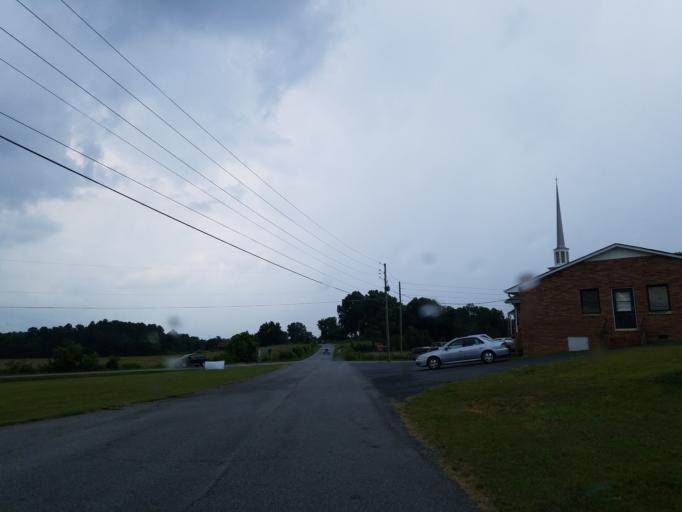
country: US
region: Georgia
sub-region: Bartow County
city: Rydal
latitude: 34.2725
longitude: -84.7563
